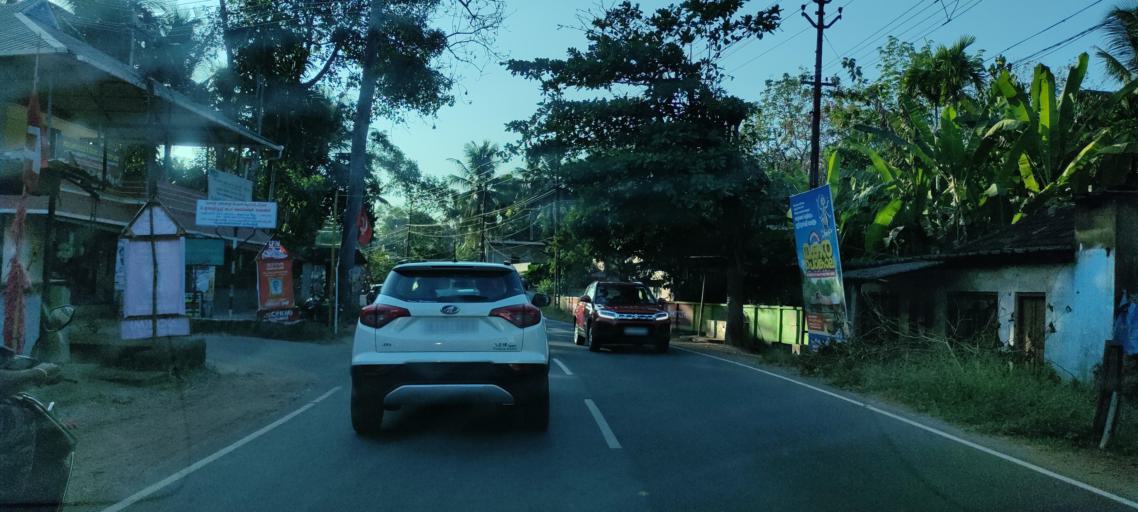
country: IN
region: Kerala
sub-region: Alappuzha
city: Kattanam
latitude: 9.1742
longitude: 76.5818
